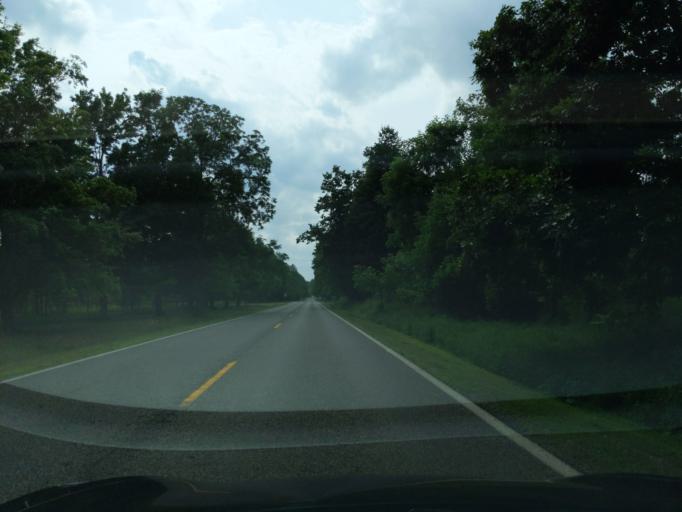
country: US
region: Michigan
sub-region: Eaton County
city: Eaton Rapids
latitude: 42.4945
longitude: -84.6336
